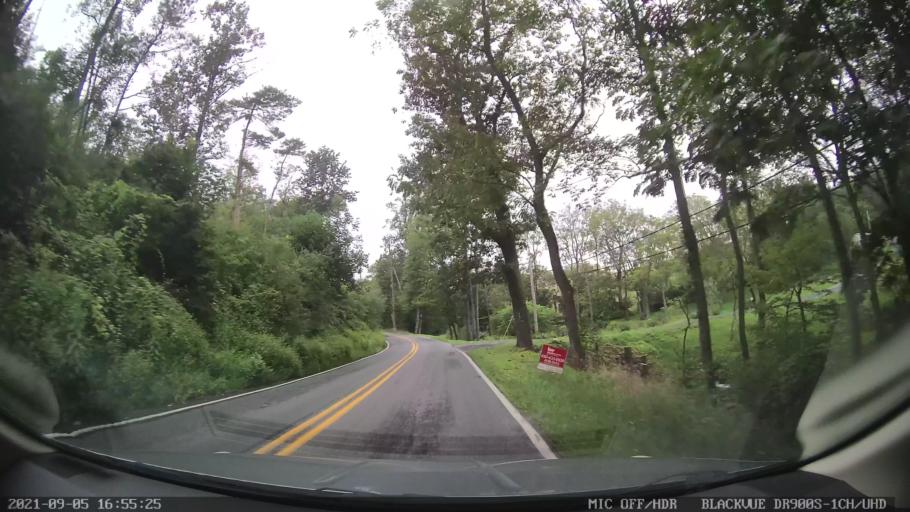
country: US
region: Pennsylvania
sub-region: Lehigh County
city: Wescosville
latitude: 40.6118
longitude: -75.5881
